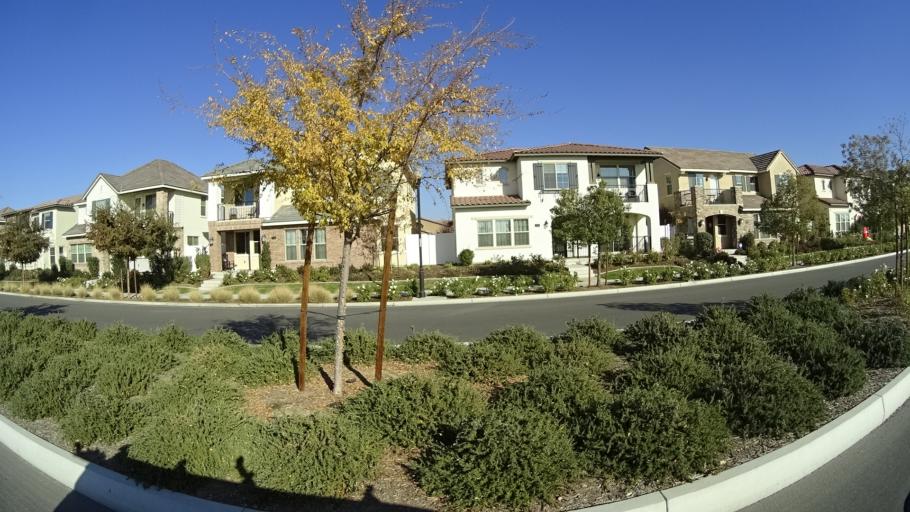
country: US
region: California
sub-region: Kern County
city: Rosedale
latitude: 35.3211
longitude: -119.1359
